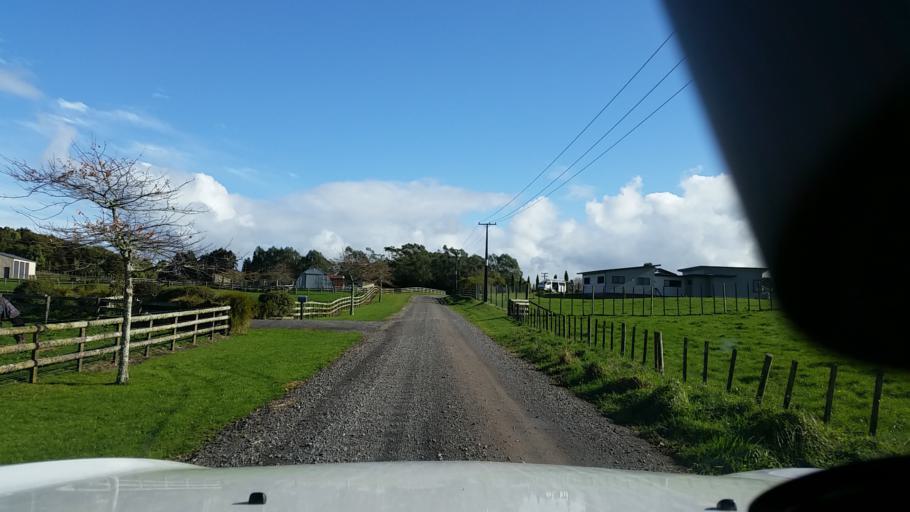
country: NZ
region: Bay of Plenty
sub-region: Rotorua District
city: Rotorua
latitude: -38.0248
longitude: 176.2816
